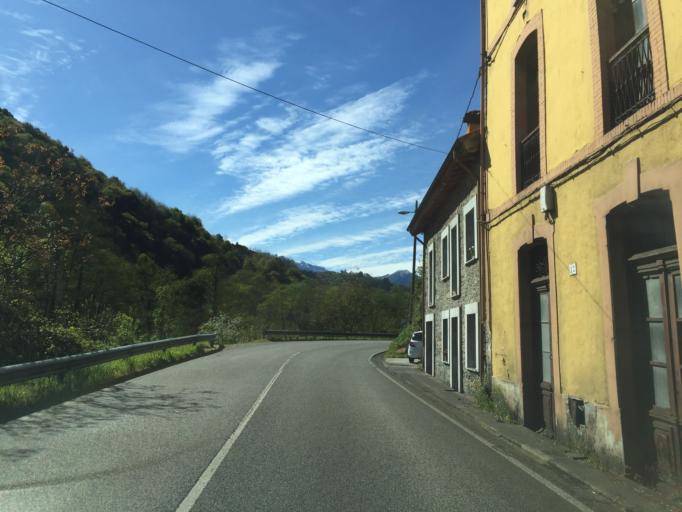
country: ES
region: Asturias
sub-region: Province of Asturias
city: Proaza
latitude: 43.3358
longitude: -5.9865
